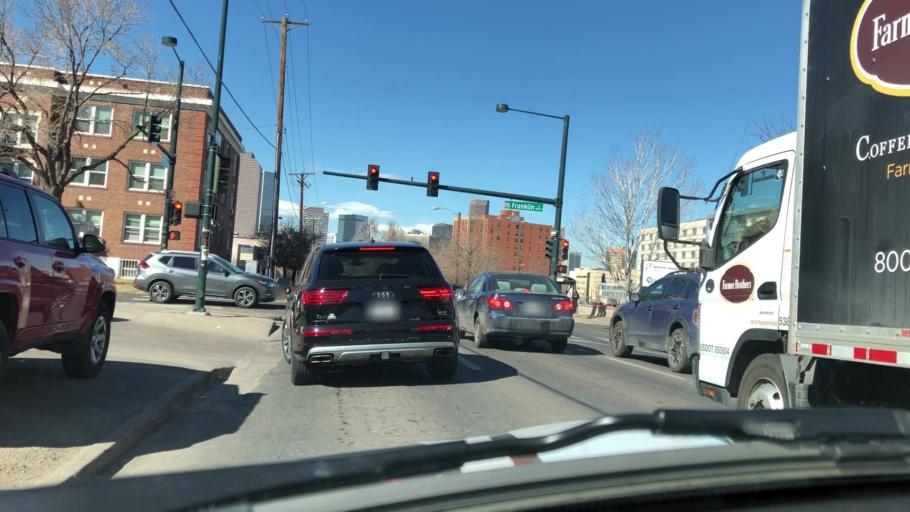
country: US
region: Colorado
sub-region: Denver County
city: Denver
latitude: 39.7448
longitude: -104.9681
